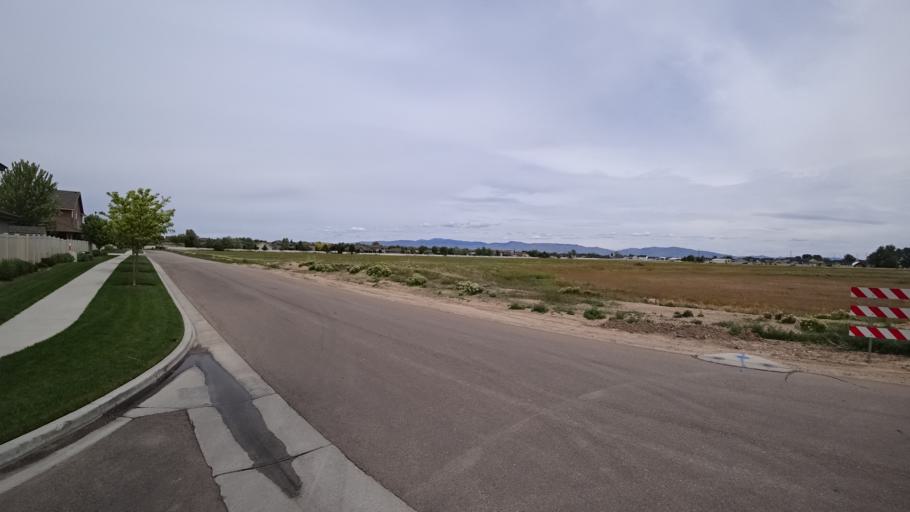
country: US
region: Idaho
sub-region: Ada County
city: Meridian
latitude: 43.5627
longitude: -116.3597
